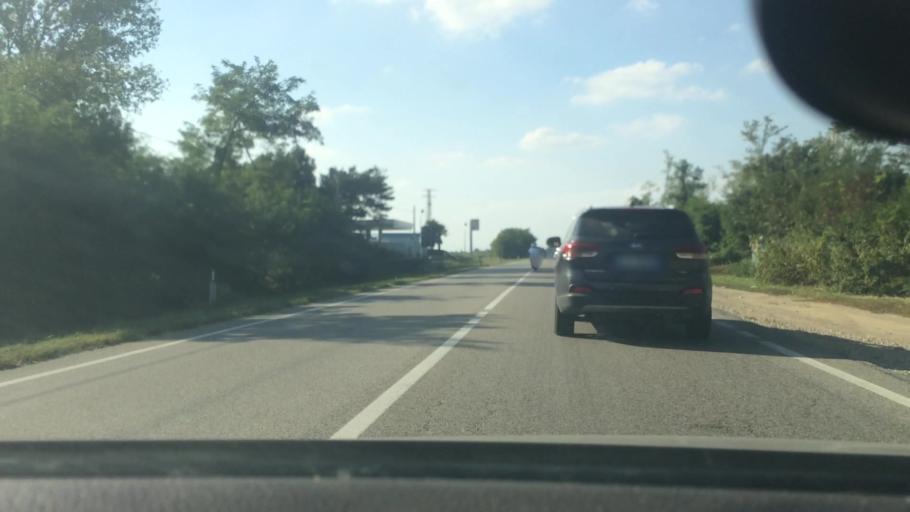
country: IT
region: Lombardy
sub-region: Citta metropolitana di Milano
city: Arconate
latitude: 45.5316
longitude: 8.8325
